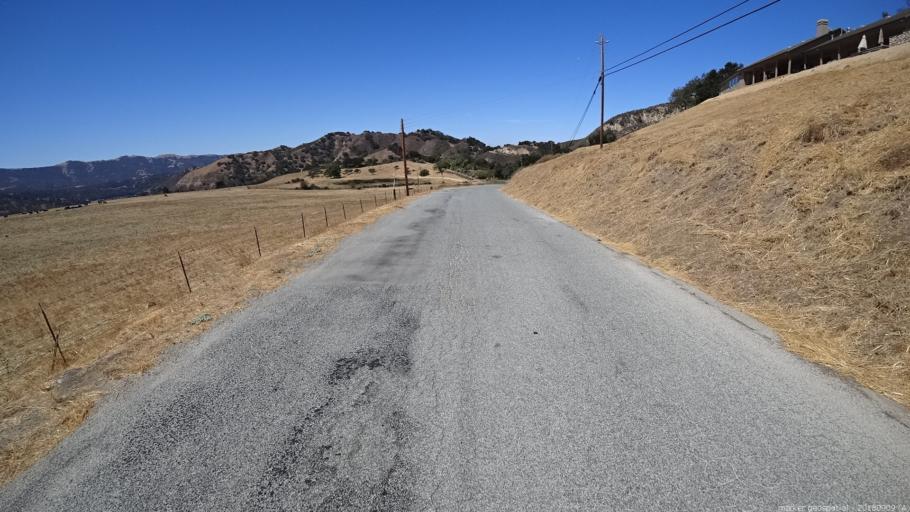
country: US
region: California
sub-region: Monterey County
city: Carmel Valley Village
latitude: 36.5413
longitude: -121.6592
